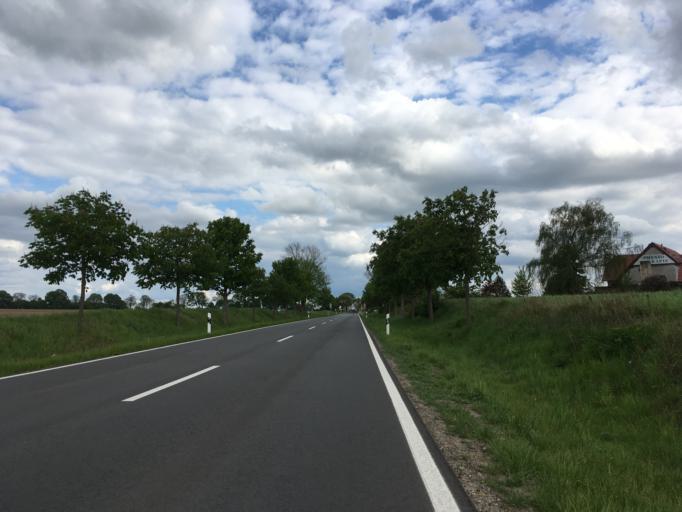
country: DE
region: Brandenburg
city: Bernau bei Berlin
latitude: 52.6585
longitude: 13.5994
